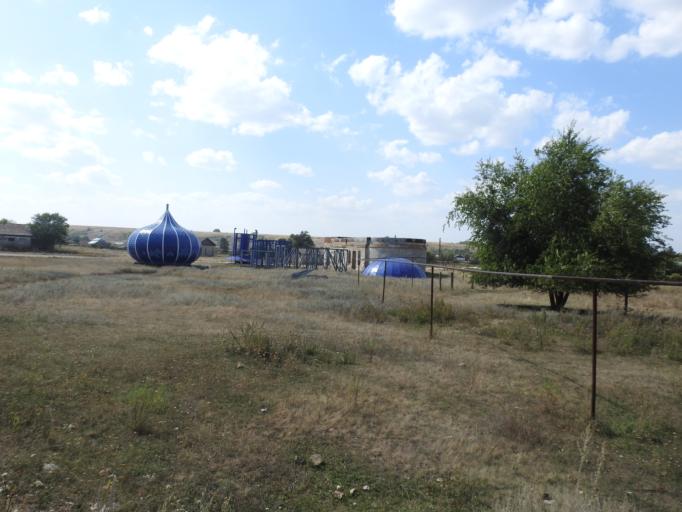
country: RU
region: Volgograd
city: Zhirnovsk
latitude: 51.2159
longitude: 44.9571
